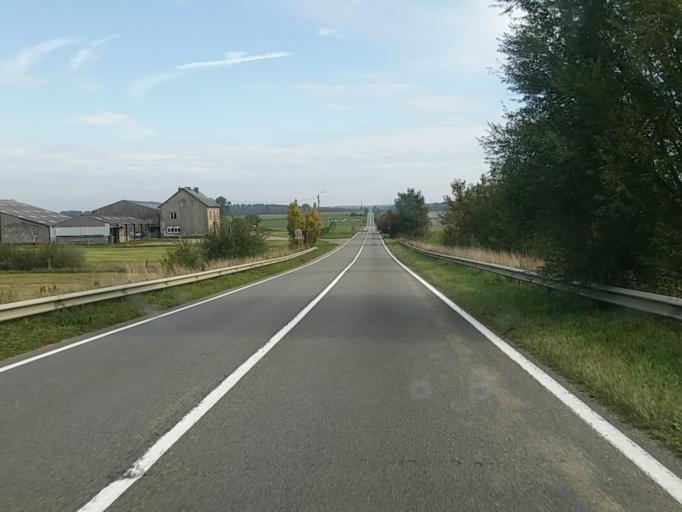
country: BE
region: Wallonia
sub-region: Province du Luxembourg
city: Etalle
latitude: 49.6819
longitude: 5.6048
